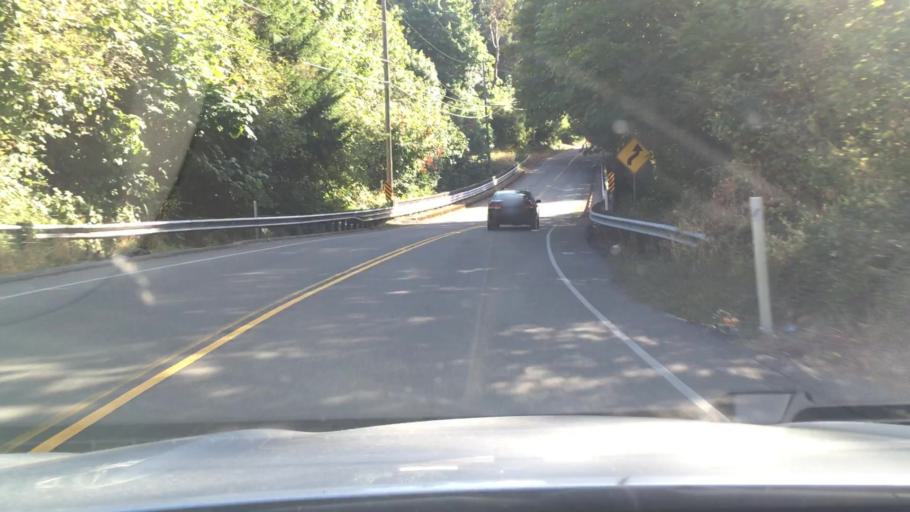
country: US
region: Washington
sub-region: Pierce County
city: Tacoma
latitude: 47.3089
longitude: -122.4318
